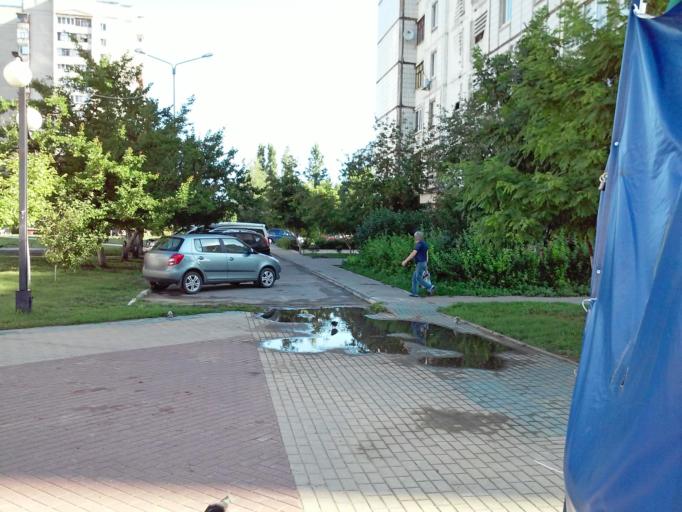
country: RU
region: Belgorod
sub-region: Belgorodskiy Rayon
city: Belgorod
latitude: 50.5607
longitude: 36.5671
